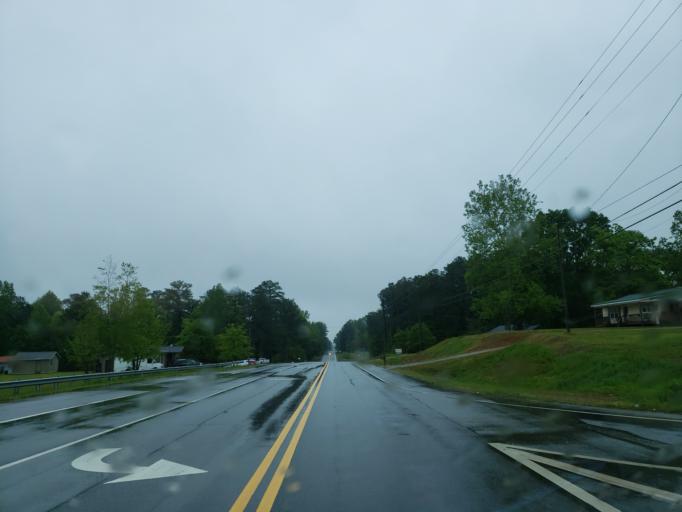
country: US
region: Georgia
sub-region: Carroll County
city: Villa Rica
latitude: 33.8218
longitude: -84.8792
